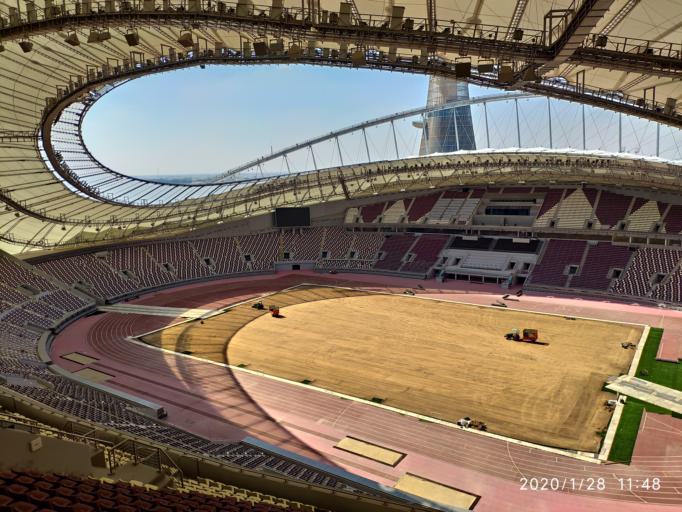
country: QA
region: Baladiyat ar Rayyan
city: Ar Rayyan
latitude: 25.2642
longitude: 51.4492
